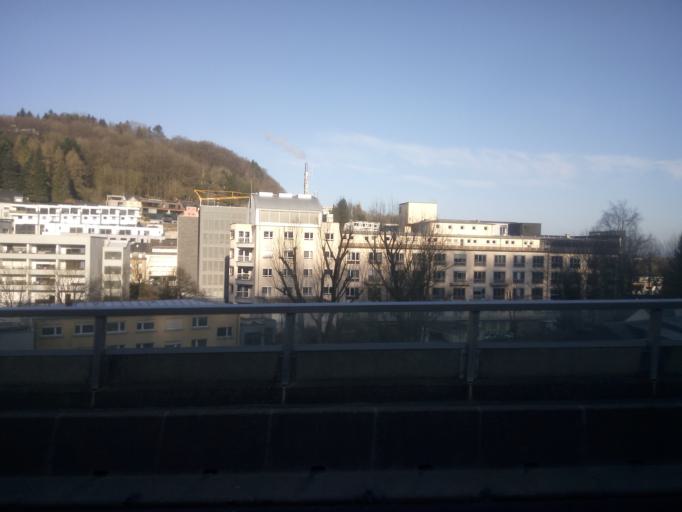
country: LU
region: Luxembourg
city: Kirchberg
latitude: 49.6307
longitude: 6.1360
